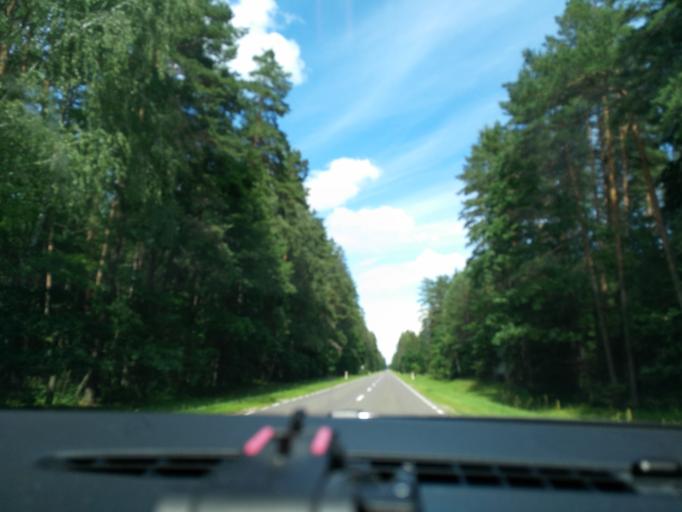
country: PL
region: Podlasie
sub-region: Powiat sejnenski
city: Sejny
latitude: 53.9856
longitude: 23.2981
